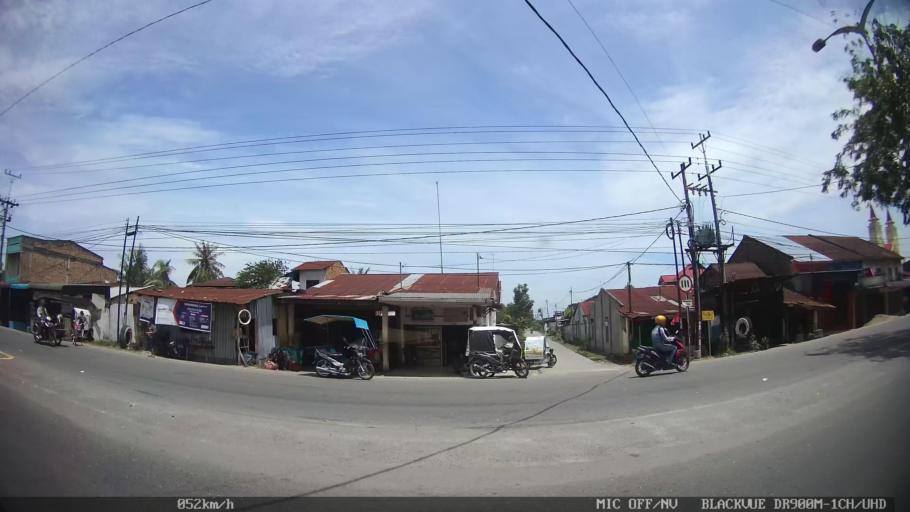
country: ID
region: North Sumatra
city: Percut
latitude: 3.5550
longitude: 98.8816
